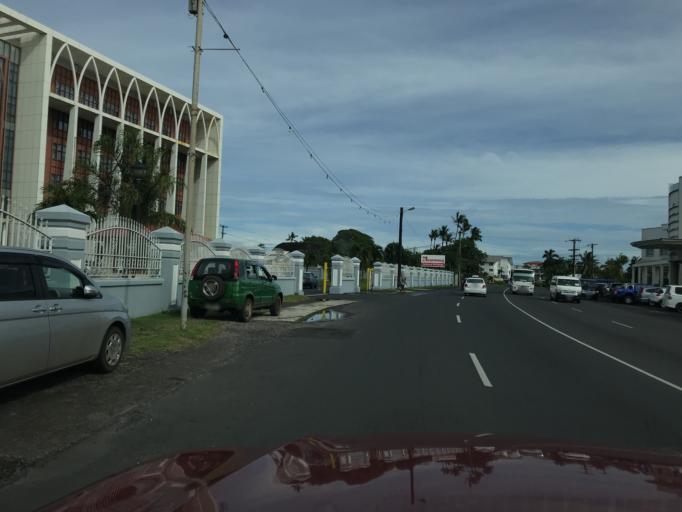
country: WS
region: Tuamasaga
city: Apia
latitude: -13.8294
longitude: -171.7718
